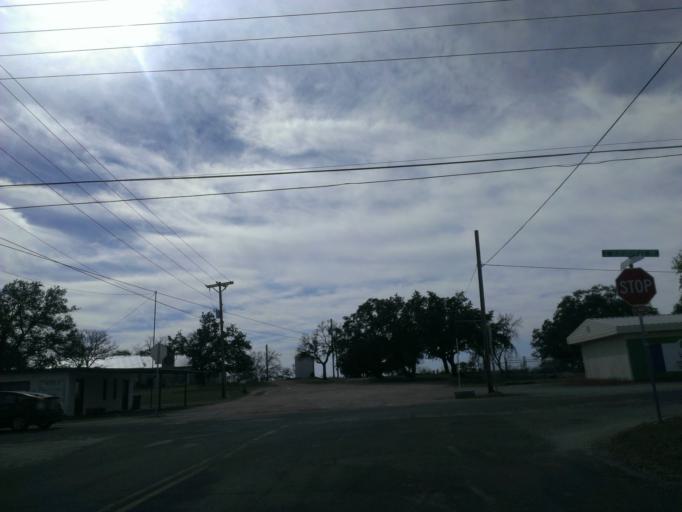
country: US
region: Texas
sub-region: Burnet County
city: Granite Shoals
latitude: 30.5891
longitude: -98.3863
